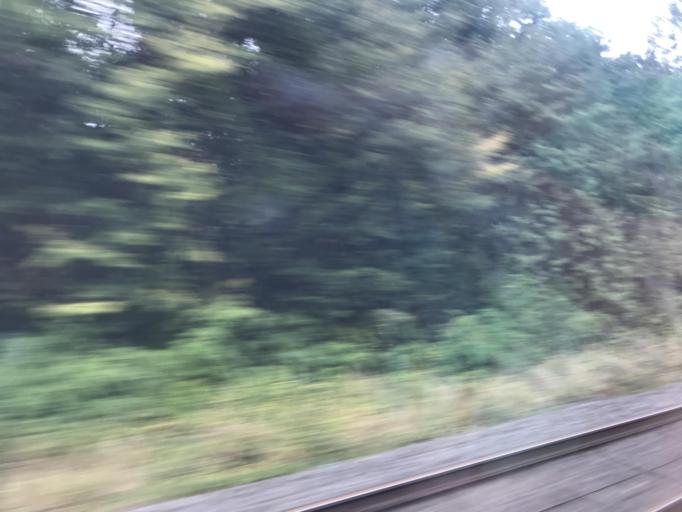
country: DE
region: North Rhine-Westphalia
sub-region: Regierungsbezirk Koln
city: Kerpen
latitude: 50.9118
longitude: 6.7019
